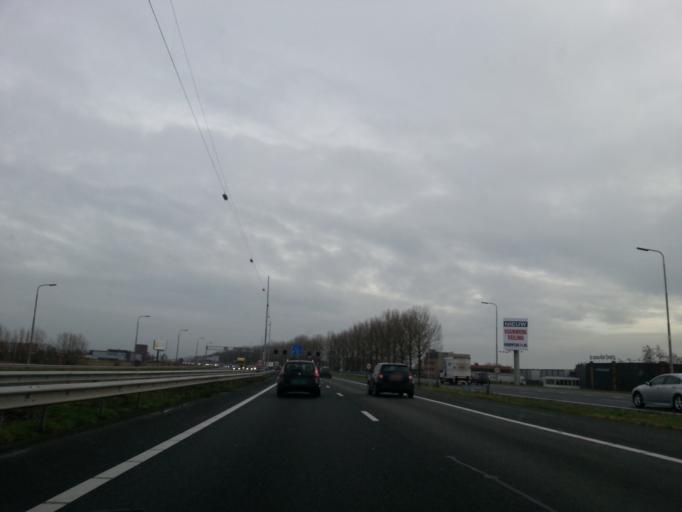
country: NL
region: Gelderland
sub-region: Gemeente Duiven
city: Duiven
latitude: 51.9678
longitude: 5.9992
